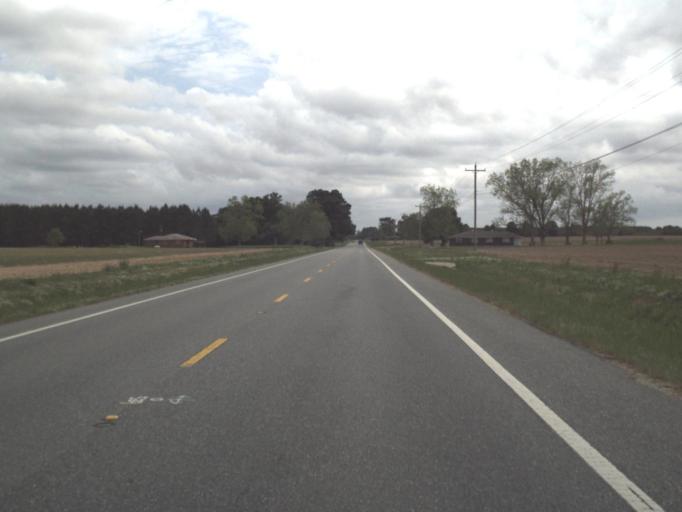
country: US
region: Florida
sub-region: Santa Rosa County
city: Point Baker
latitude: 30.8662
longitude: -87.0526
